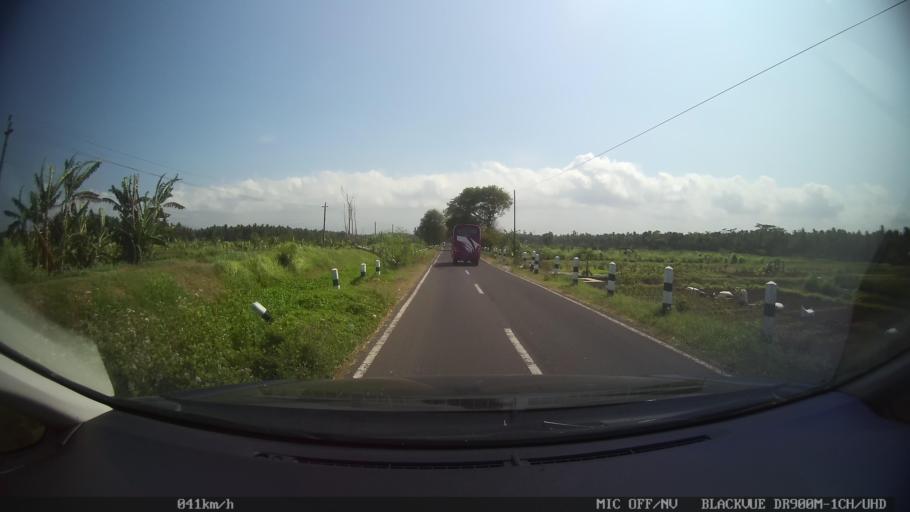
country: ID
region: Daerah Istimewa Yogyakarta
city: Srandakan
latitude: -7.9351
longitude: 110.1555
